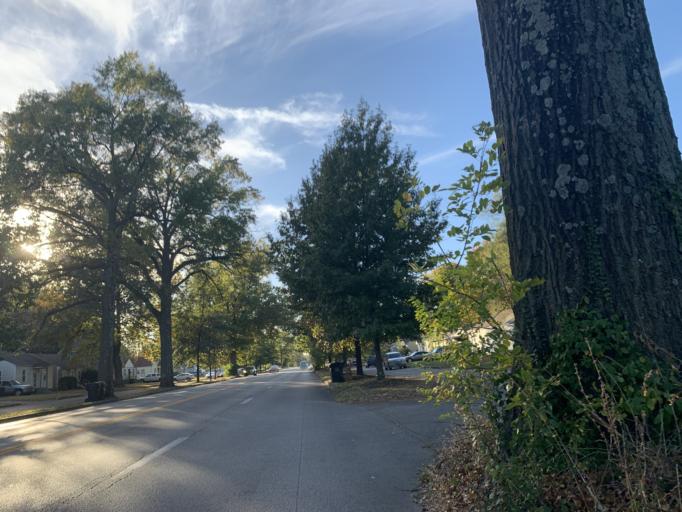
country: US
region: Kentucky
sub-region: Jefferson County
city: Shively
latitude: 38.2241
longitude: -85.8054
